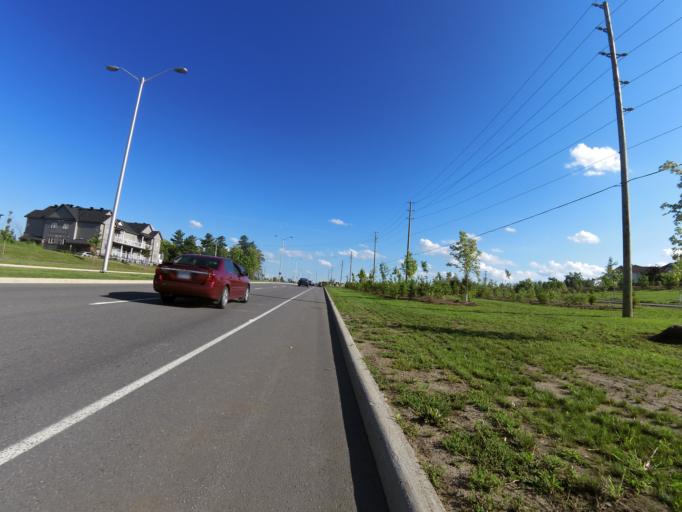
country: CA
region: Ontario
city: Clarence-Rockland
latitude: 45.4860
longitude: -75.4756
